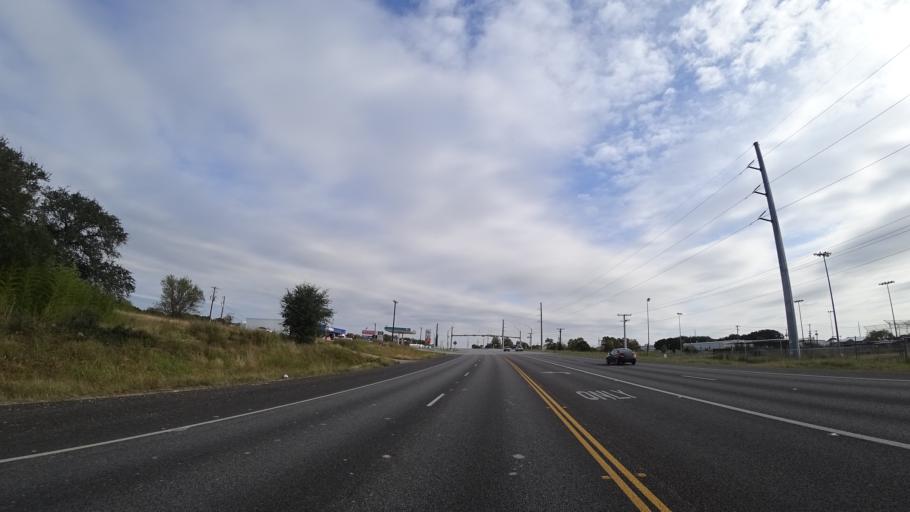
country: US
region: Texas
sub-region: Travis County
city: Manchaca
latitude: 30.1336
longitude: -97.8543
